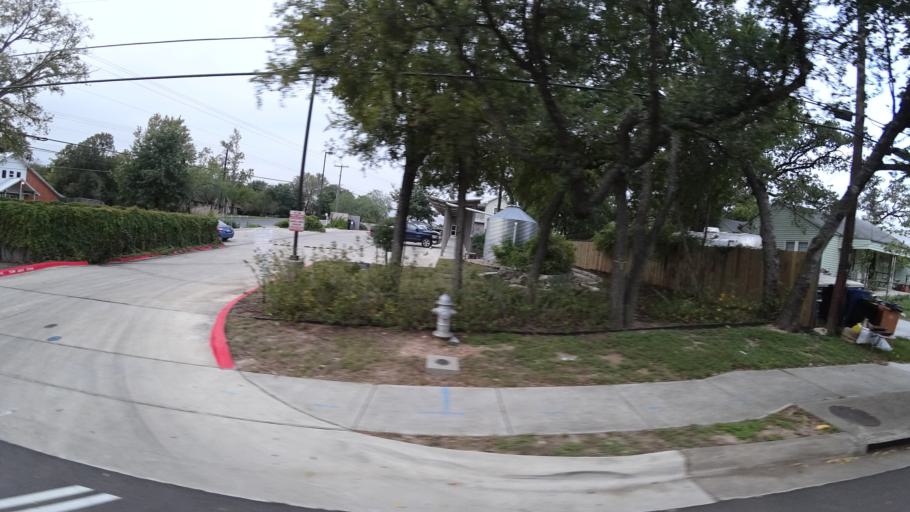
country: US
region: Texas
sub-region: Travis County
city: Austin
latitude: 30.2841
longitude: -97.6964
